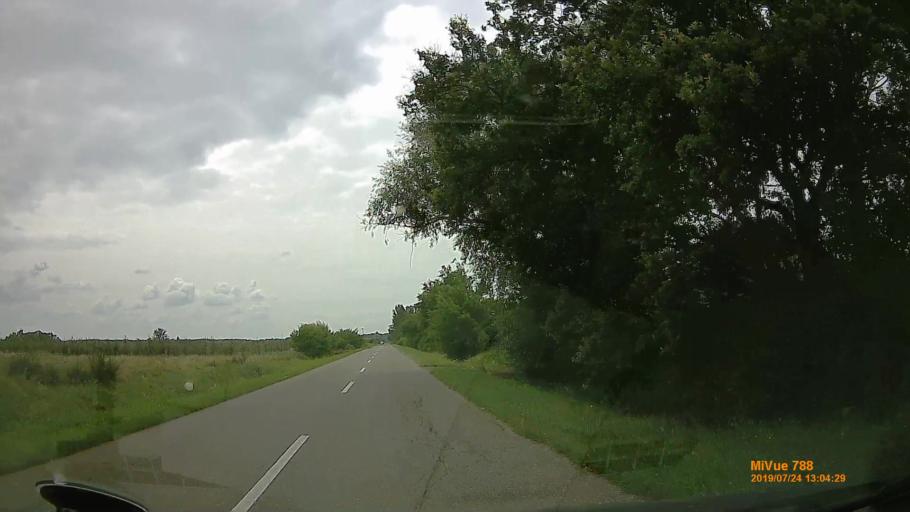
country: HU
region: Szabolcs-Szatmar-Bereg
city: Aranyosapati
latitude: 48.2019
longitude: 22.3059
